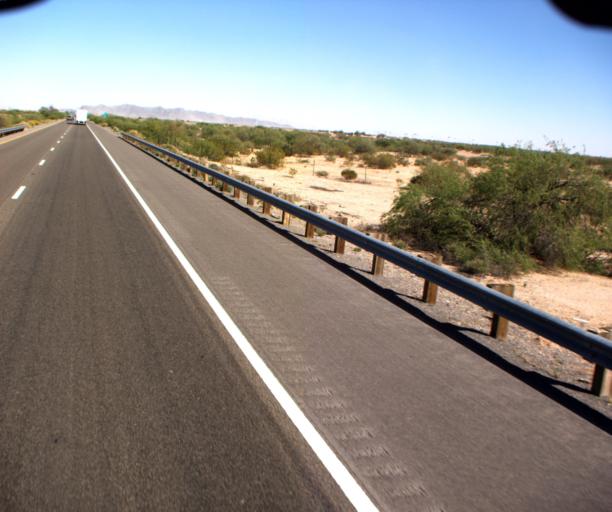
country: US
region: Arizona
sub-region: Pinal County
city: Casa Grande
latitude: 32.8279
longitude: -111.8446
